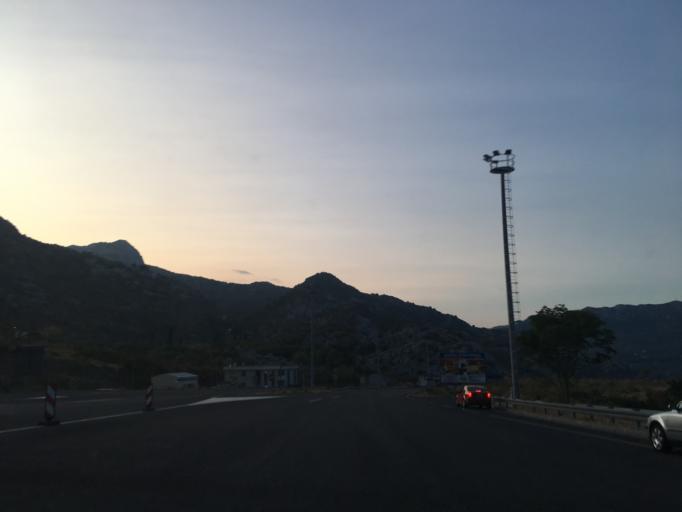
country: ME
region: Bar
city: Sutomore
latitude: 42.2013
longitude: 19.0515
